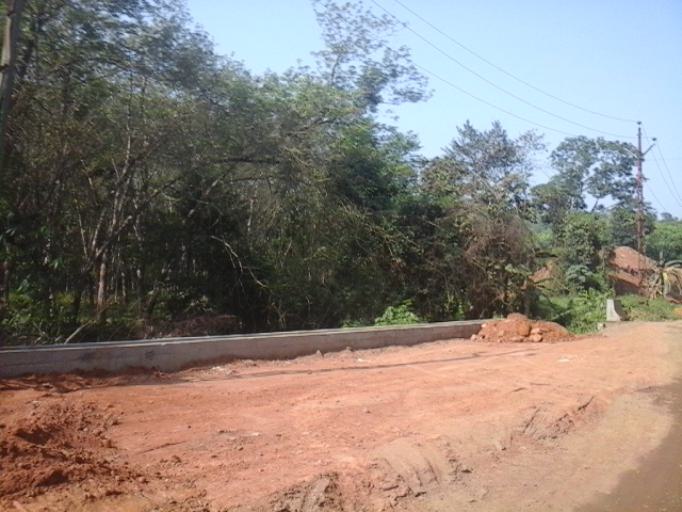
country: IN
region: Kerala
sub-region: Kottayam
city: Lalam
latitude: 9.6871
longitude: 76.6929
